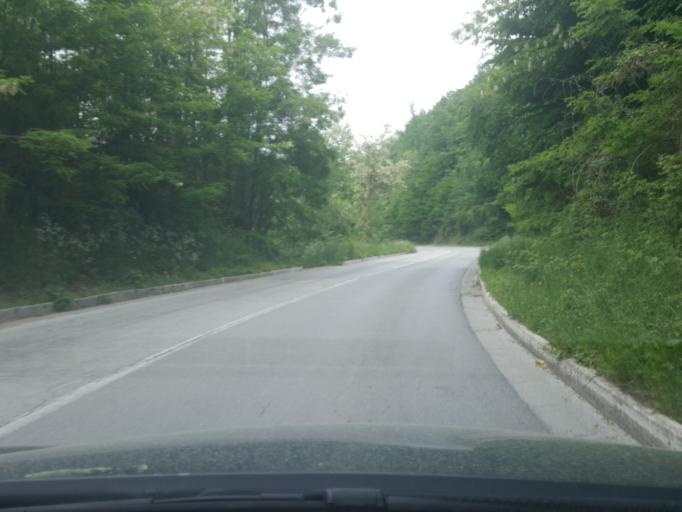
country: RS
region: Central Serbia
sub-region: Zlatiborski Okrug
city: Bajina Basta
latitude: 43.9381
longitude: 19.5699
